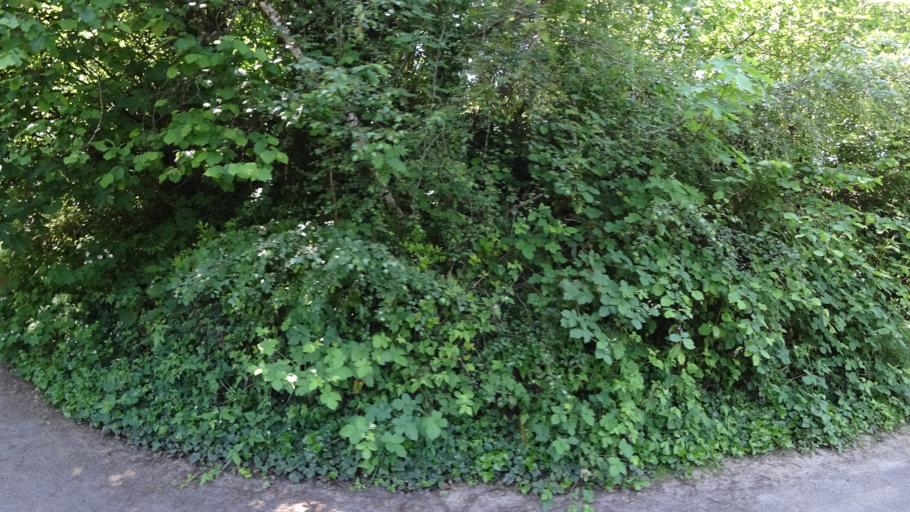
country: US
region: Oregon
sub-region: Multnomah County
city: Portland
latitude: 45.4951
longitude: -122.6989
